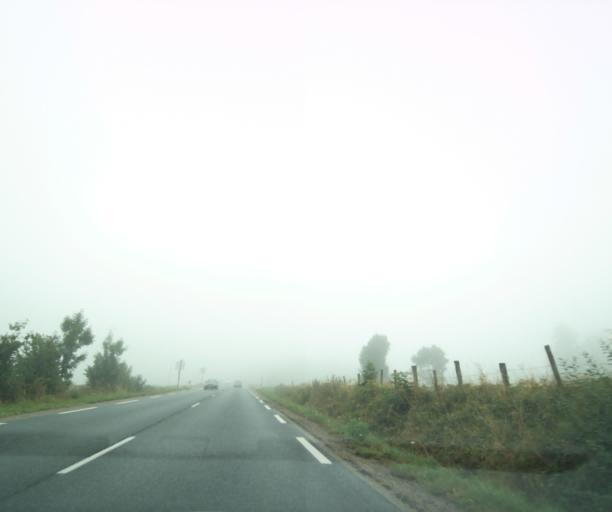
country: FR
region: Midi-Pyrenees
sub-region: Departement de l'Aveyron
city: Baraqueville
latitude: 44.2621
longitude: 2.4174
